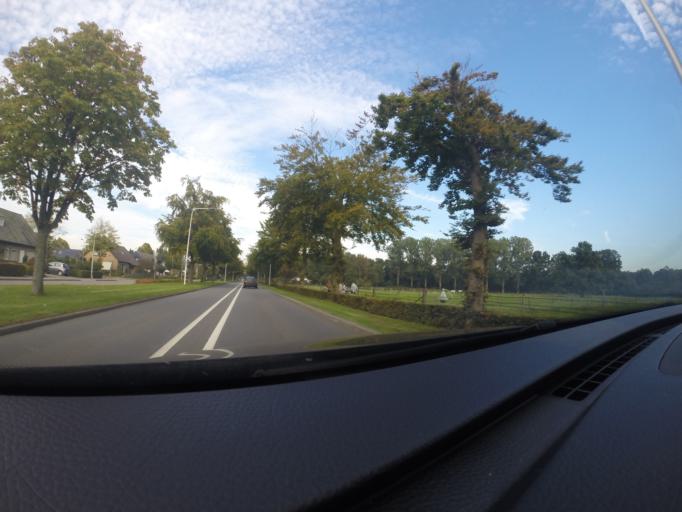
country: NL
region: Gelderland
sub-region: Gemeente Bronckhorst
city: Hengelo
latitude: 52.0982
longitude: 6.3129
